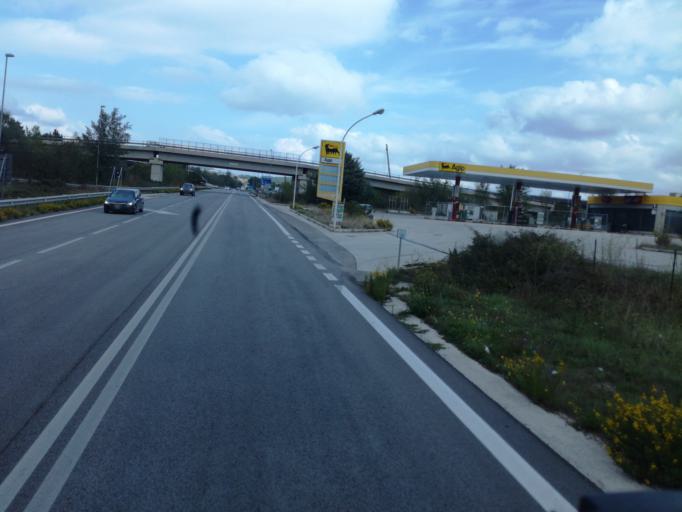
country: IT
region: Molise
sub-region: Provincia di Campobasso
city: Guardiaregia
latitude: 41.4667
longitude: 14.5593
